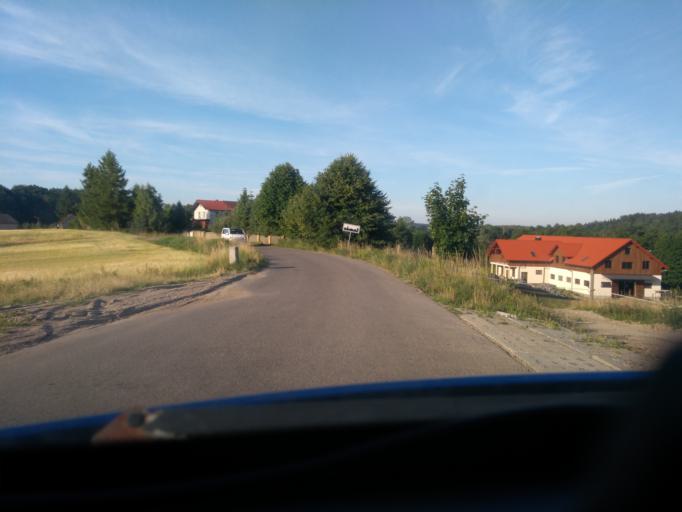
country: PL
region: Pomeranian Voivodeship
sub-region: Powiat kartuski
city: Przodkowo
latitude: 54.3834
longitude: 18.3168
